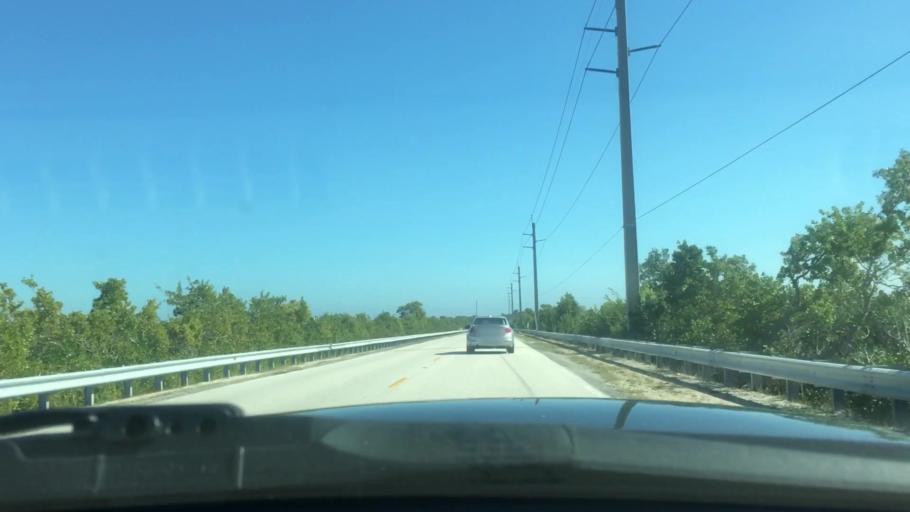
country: US
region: Florida
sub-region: Monroe County
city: North Key Largo
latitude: 25.2847
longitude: -80.3093
